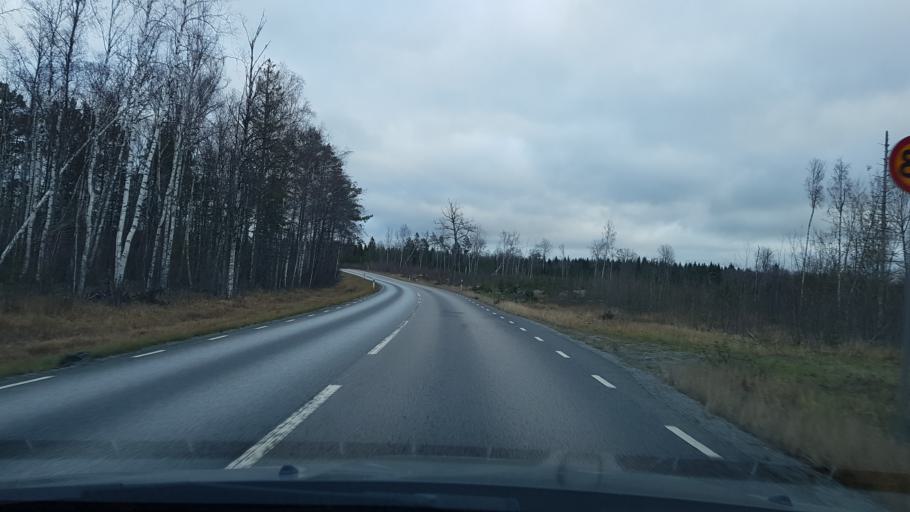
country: SE
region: Stockholm
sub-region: Norrtalje Kommun
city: Skanninge
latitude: 60.0298
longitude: 18.4333
